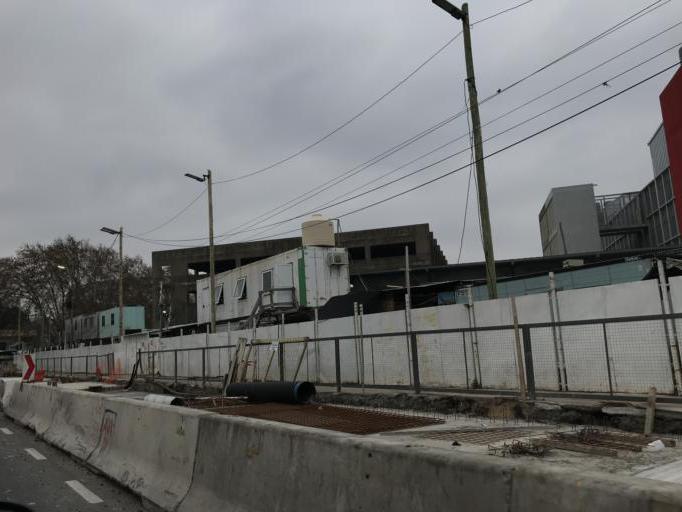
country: AR
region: Buenos Aires F.D.
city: Retiro
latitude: -34.5885
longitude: -58.3713
